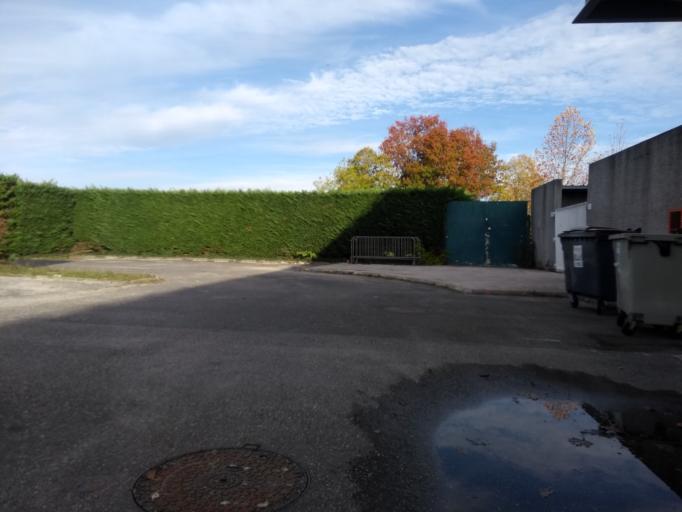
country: FR
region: Aquitaine
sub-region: Departement de la Gironde
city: Pessac
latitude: 44.8010
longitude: -0.6431
